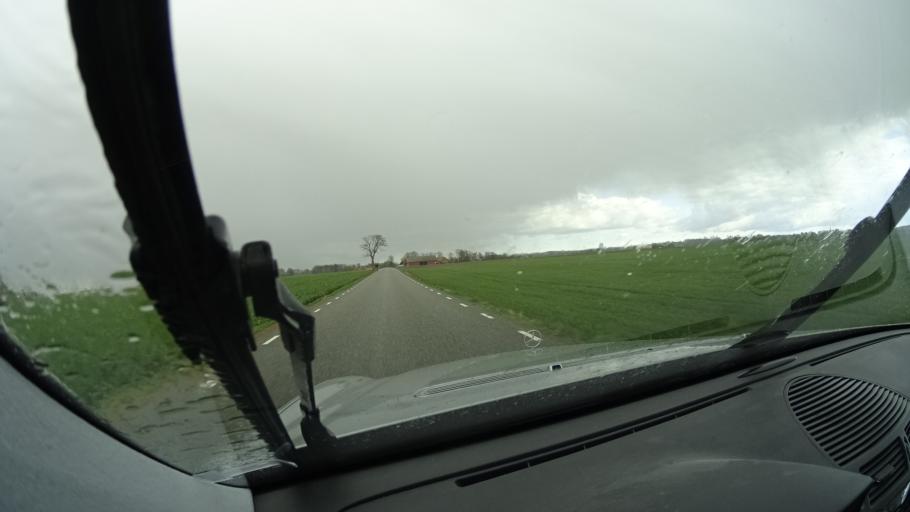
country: SE
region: Skane
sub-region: Lunds Kommun
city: Lund
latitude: 55.7439
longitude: 13.1597
